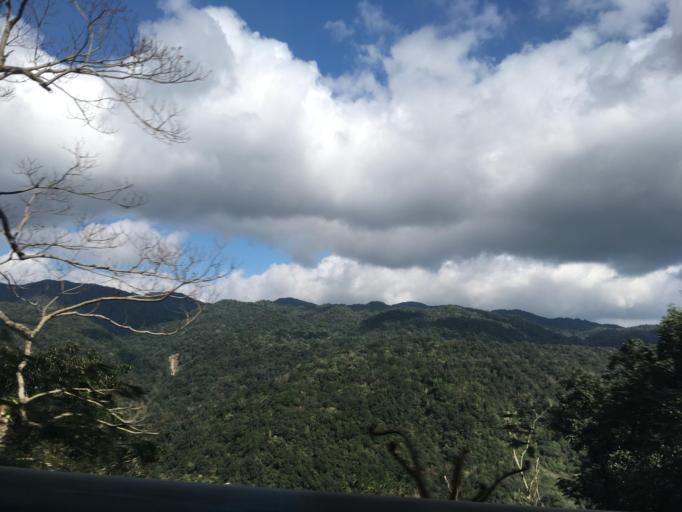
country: TW
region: Taiwan
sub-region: Yilan
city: Yilan
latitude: 24.7502
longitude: 121.6443
